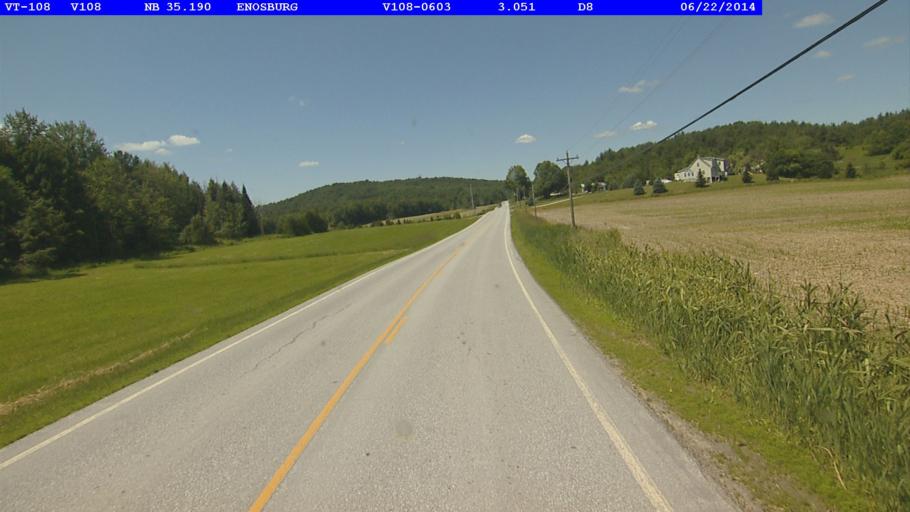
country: US
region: Vermont
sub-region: Franklin County
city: Enosburg Falls
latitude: 44.8804
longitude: -72.7981
